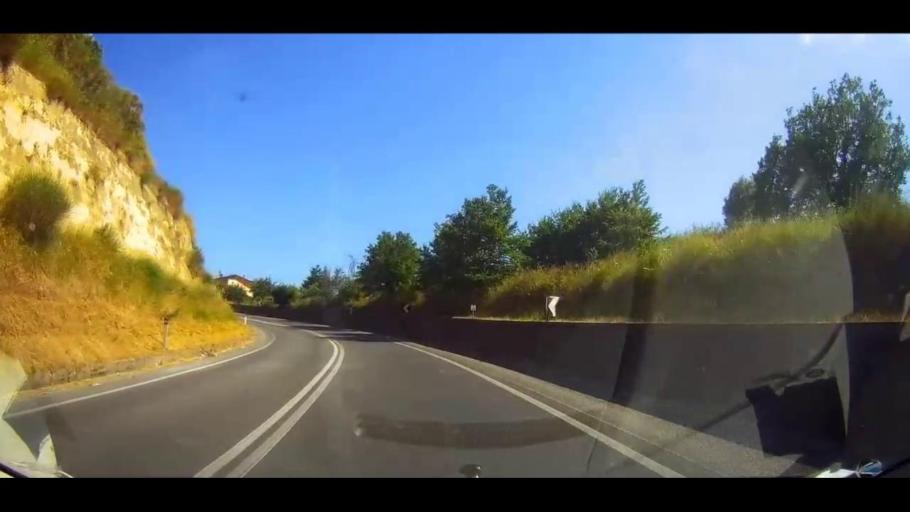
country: IT
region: Calabria
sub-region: Provincia di Cosenza
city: Cosenza
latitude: 39.2969
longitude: 16.2642
